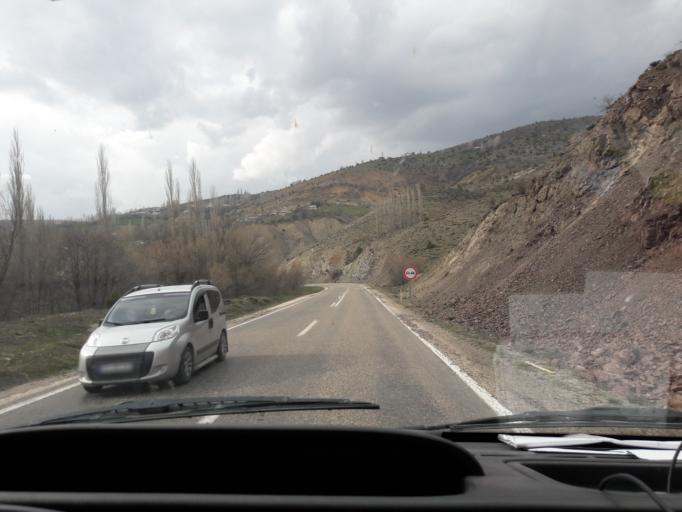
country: TR
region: Giresun
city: Alucra
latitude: 40.2691
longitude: 38.8840
